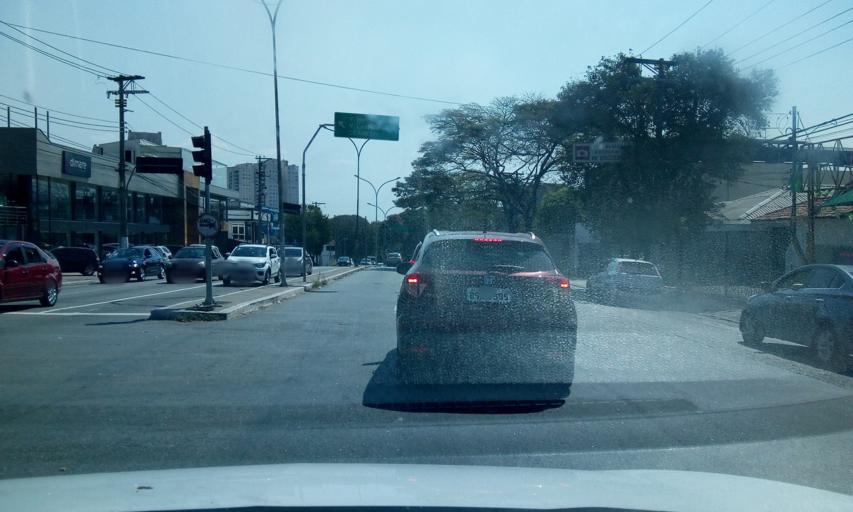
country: BR
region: Sao Paulo
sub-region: Osasco
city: Osasco
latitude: -23.5213
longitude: -46.7194
